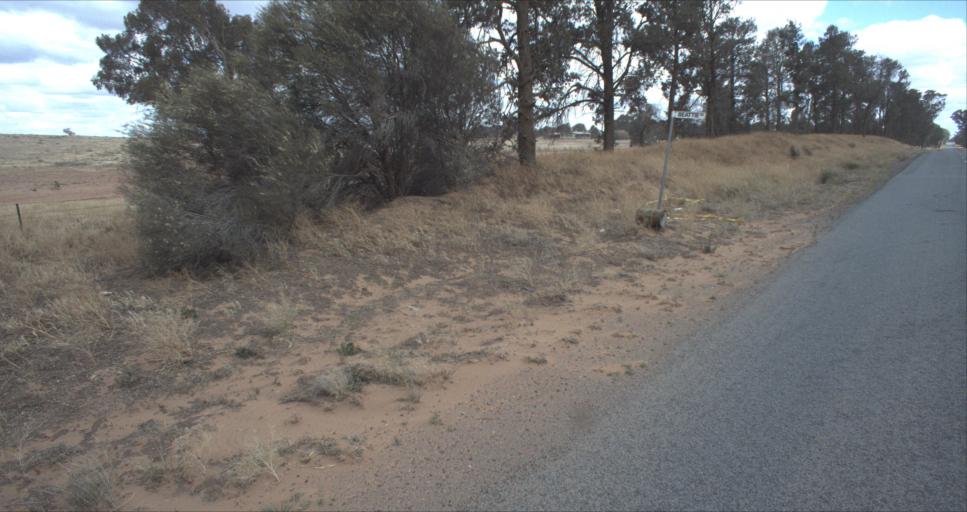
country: AU
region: New South Wales
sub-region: Leeton
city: Leeton
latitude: -34.6581
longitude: 146.3499
